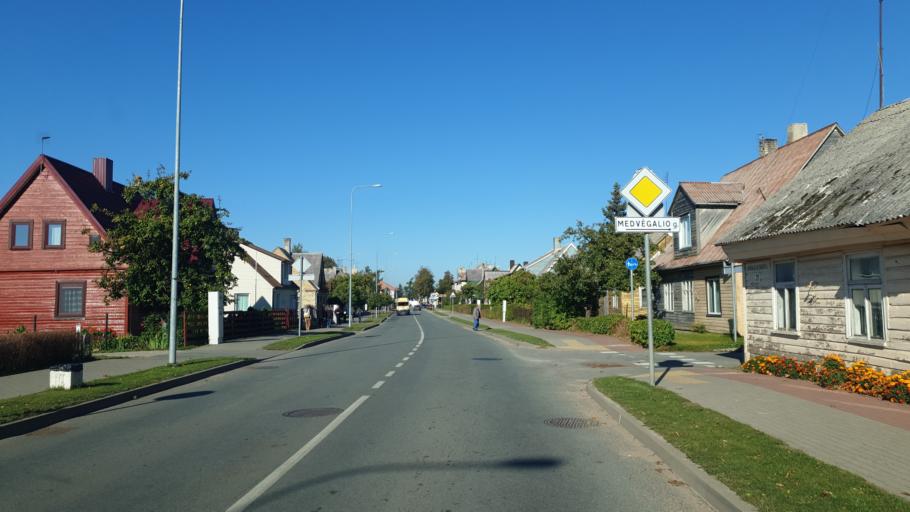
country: LT
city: Varniai
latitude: 55.7403
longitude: 22.3759
